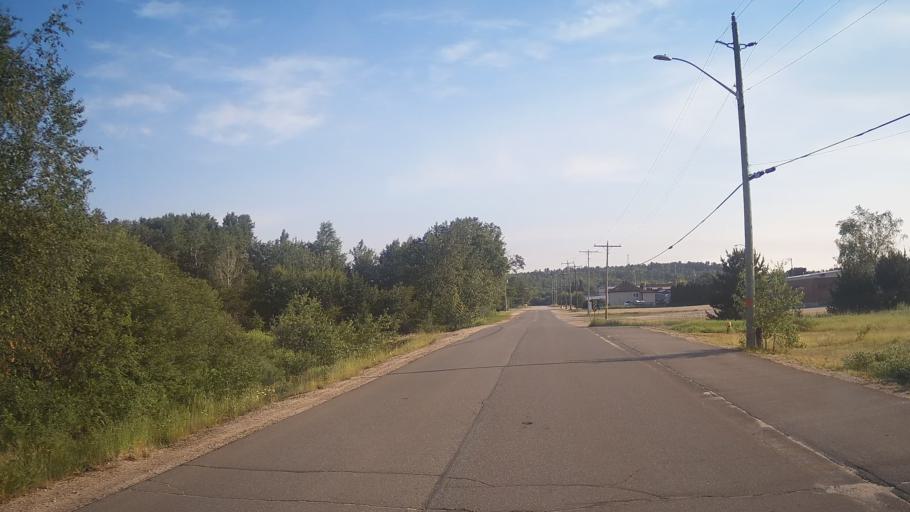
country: CA
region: Ontario
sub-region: Rainy River District
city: Atikokan
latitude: 49.4143
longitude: -91.6654
